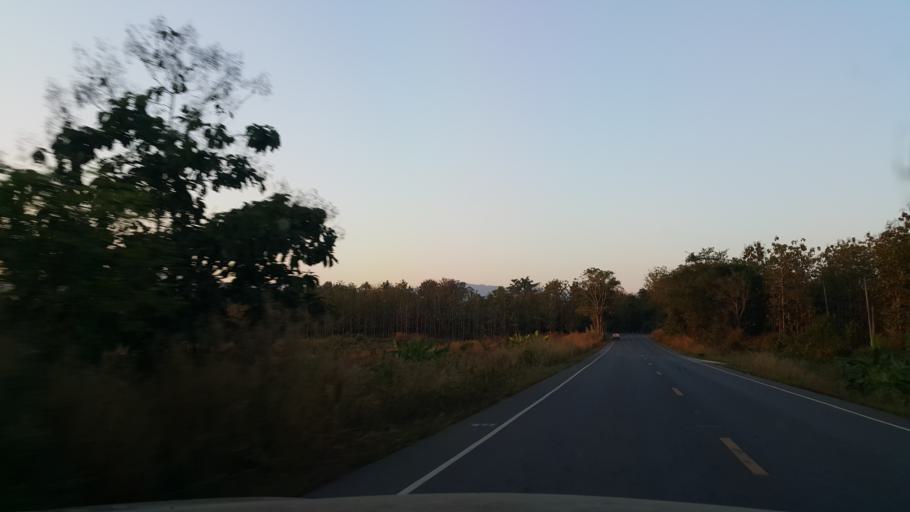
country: TH
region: Phrae
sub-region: Amphoe Wang Chin
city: Wang Chin
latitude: 17.8566
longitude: 99.6268
